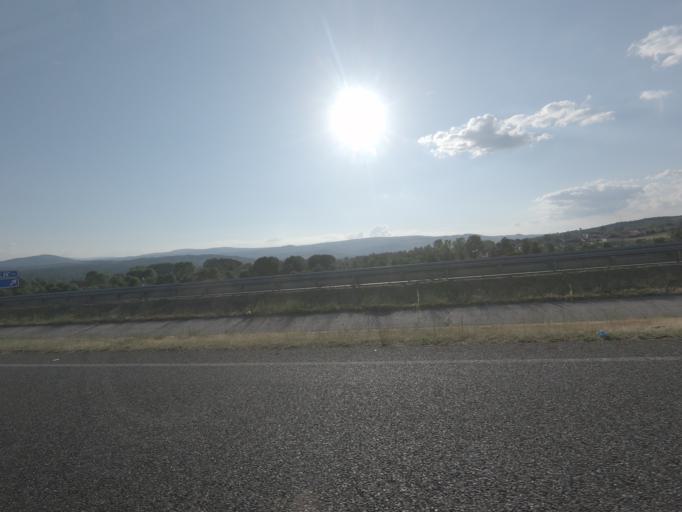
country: ES
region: Galicia
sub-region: Provincia de Ourense
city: Oimbra
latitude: 41.8448
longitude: -7.4129
